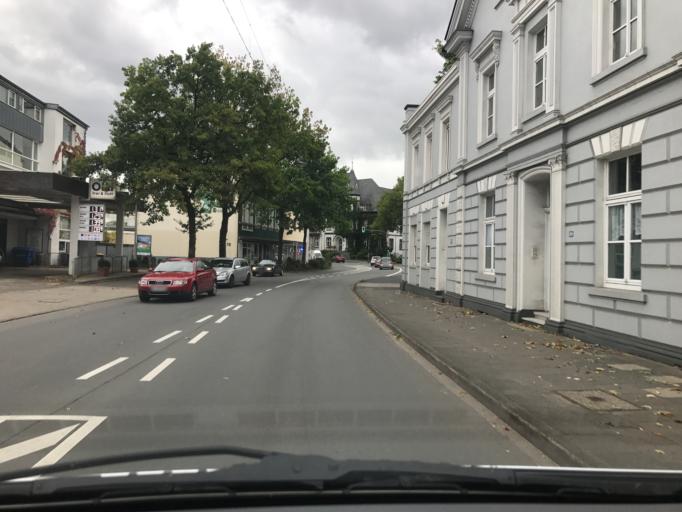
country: DE
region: North Rhine-Westphalia
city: Haan
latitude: 51.1953
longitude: 7.0149
